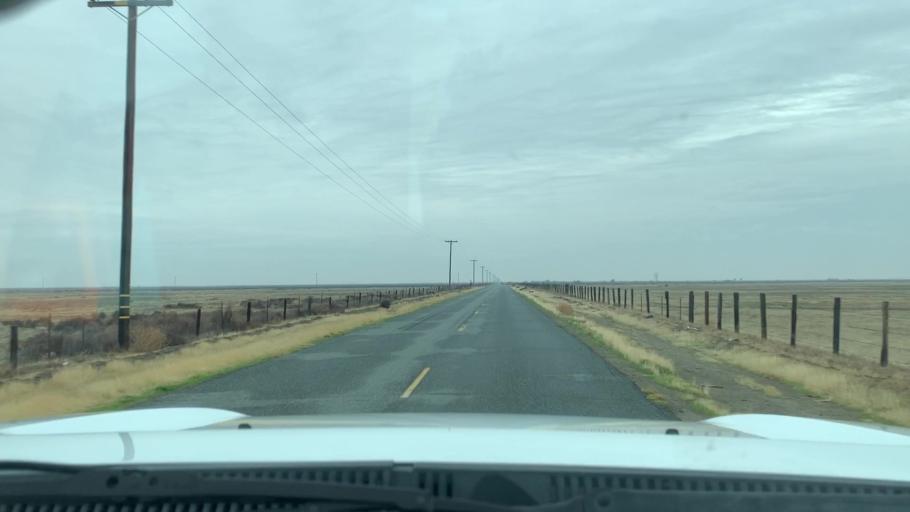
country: US
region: California
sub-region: Tulare County
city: Alpaugh
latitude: 35.7608
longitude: -119.5513
